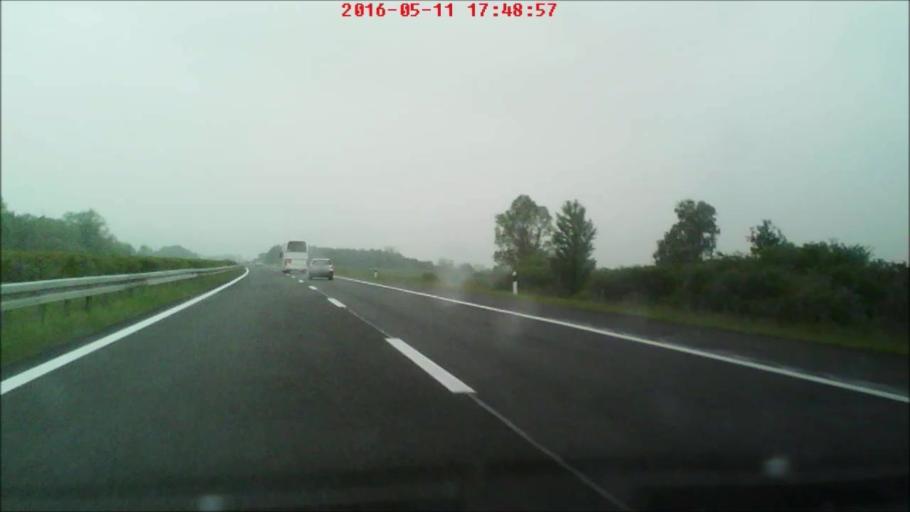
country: HR
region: Zagrebacka
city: Pojatno
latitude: 45.8981
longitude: 15.8215
